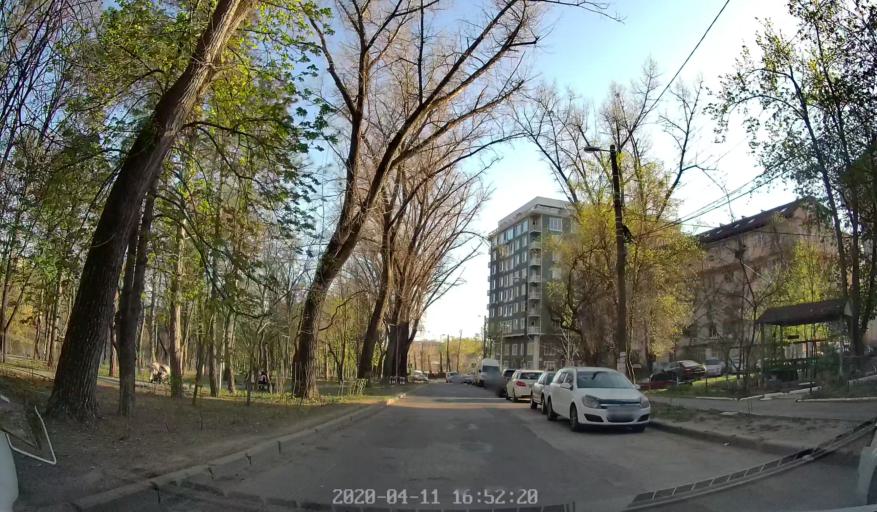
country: MD
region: Chisinau
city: Chisinau
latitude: 47.0397
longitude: 28.8692
